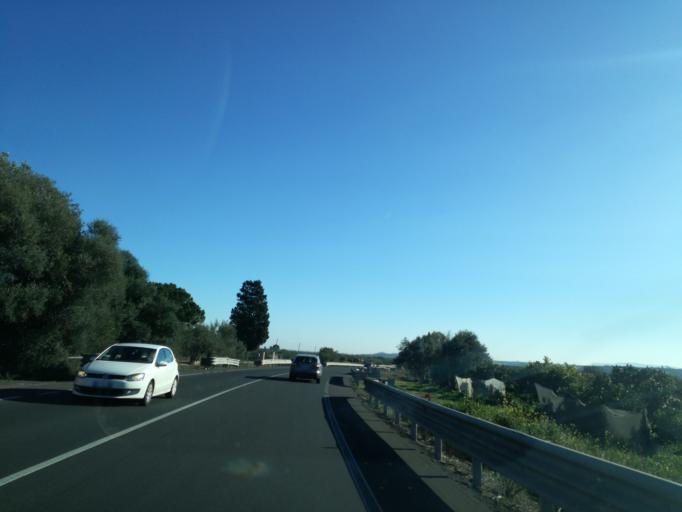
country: IT
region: Sicily
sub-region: Catania
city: Ramacca
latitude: 37.3763
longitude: 14.7310
